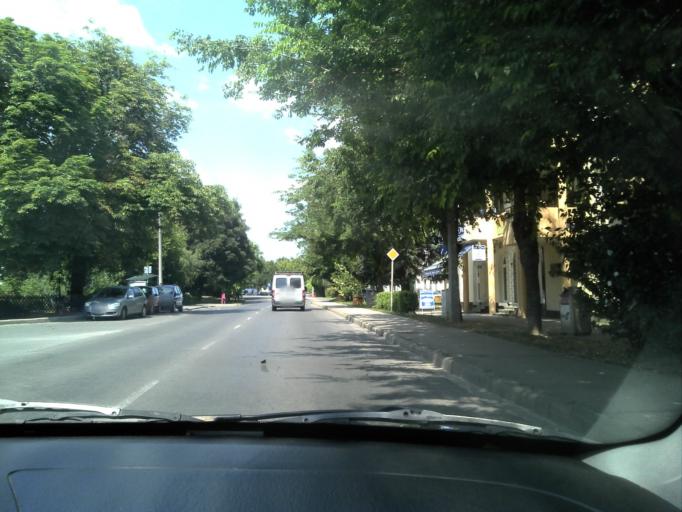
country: HU
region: Tolna
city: Tamasi
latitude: 46.6344
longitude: 18.2817
